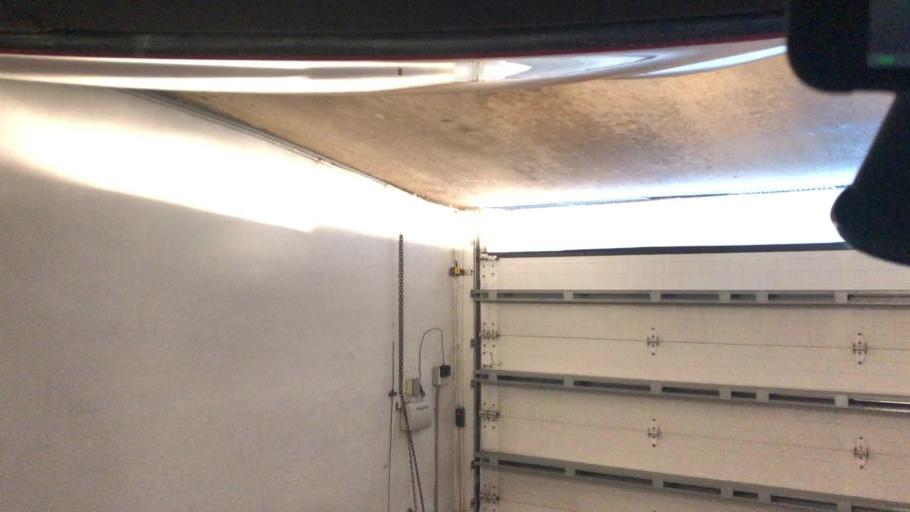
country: US
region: Florida
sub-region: Volusia County
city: Daytona Beach Shores
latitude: 29.1698
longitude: -80.9769
